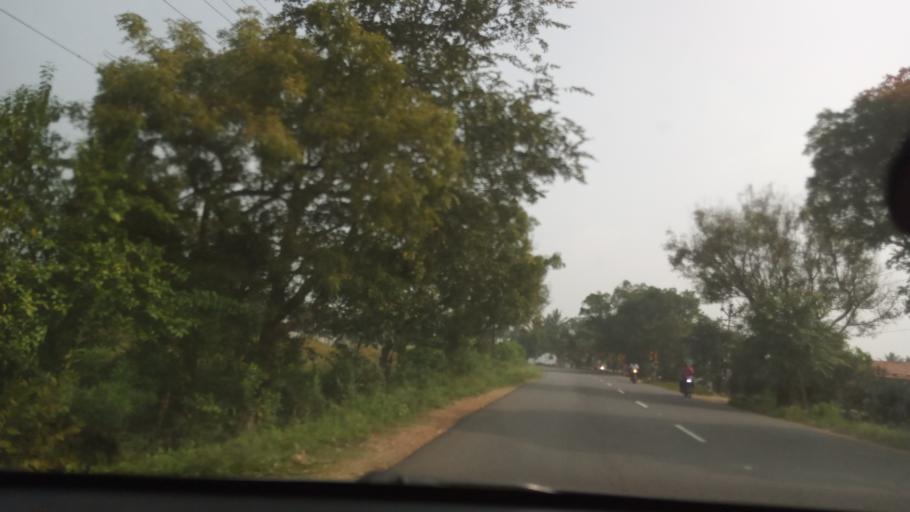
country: IN
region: Tamil Nadu
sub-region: Erode
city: Punjai Puliyampatti
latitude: 11.3302
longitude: 77.1524
